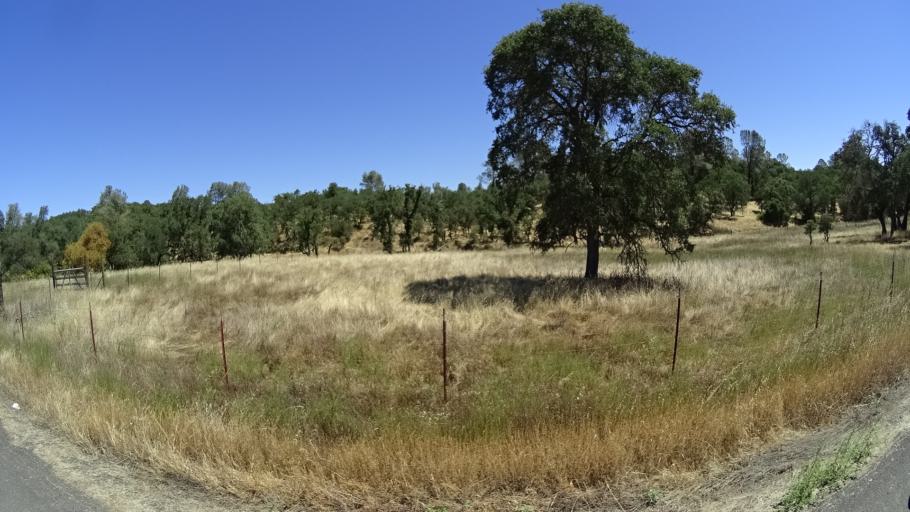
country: US
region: California
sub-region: Calaveras County
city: Copperopolis
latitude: 37.9634
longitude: -120.7030
